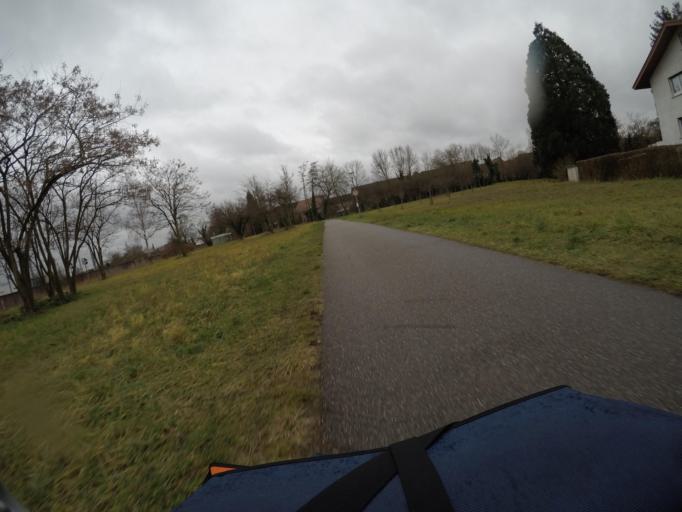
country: DE
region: Baden-Wuerttemberg
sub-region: Karlsruhe Region
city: Graben-Neudorf
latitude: 49.1586
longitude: 8.4892
